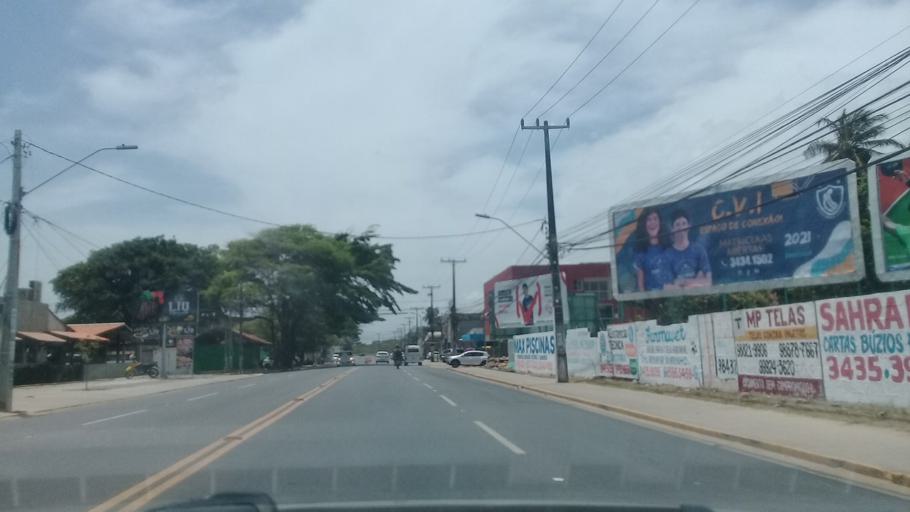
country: BR
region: Pernambuco
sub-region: Paulista
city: Paulista
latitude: -7.9533
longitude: -34.8294
